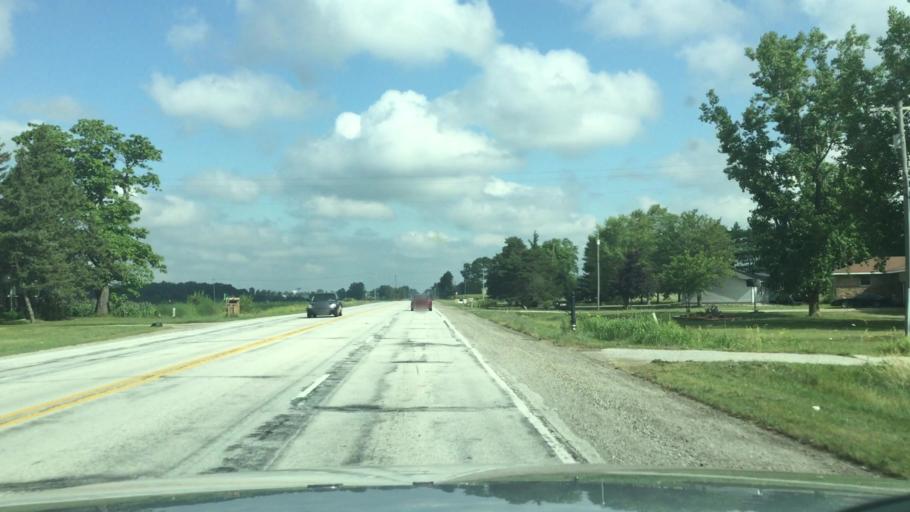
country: US
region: Michigan
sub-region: Saginaw County
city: Birch Run
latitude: 43.2331
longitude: -83.7564
